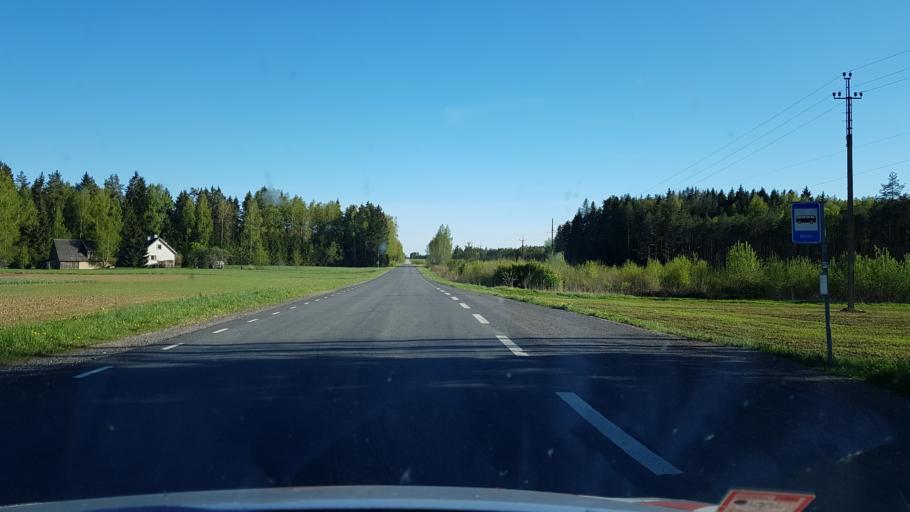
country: EE
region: Vorumaa
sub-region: Voru linn
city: Voru
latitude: 57.9423
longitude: 26.9535
